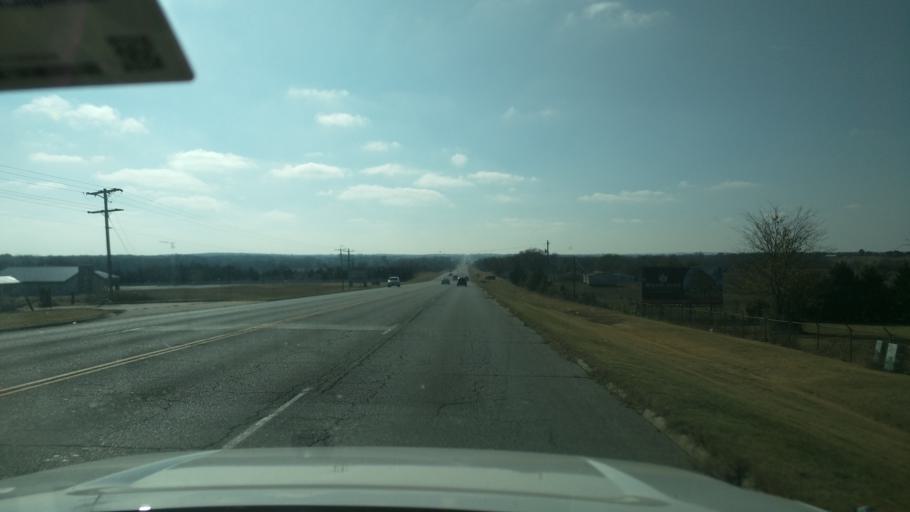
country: US
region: Oklahoma
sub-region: Washington County
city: Bartlesville
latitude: 36.6836
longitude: -95.9352
